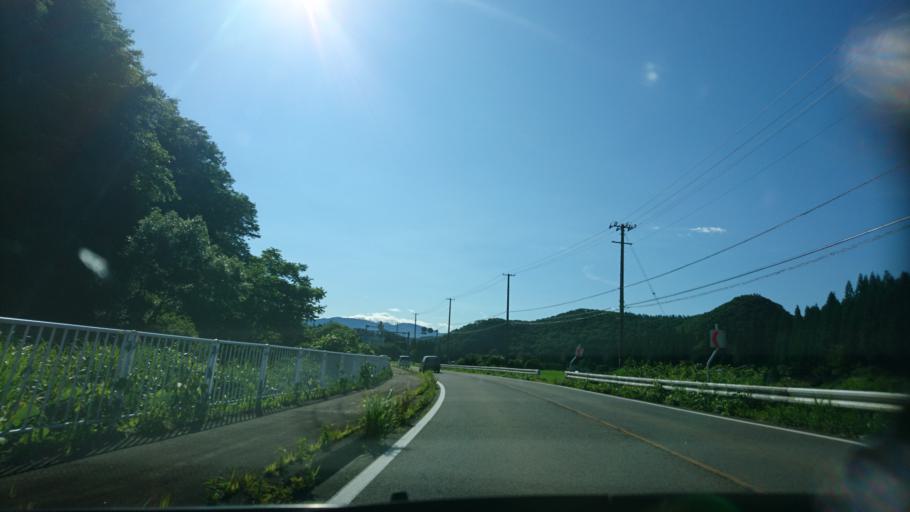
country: JP
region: Akita
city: Kakunodatemachi
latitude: 39.6153
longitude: 140.4872
